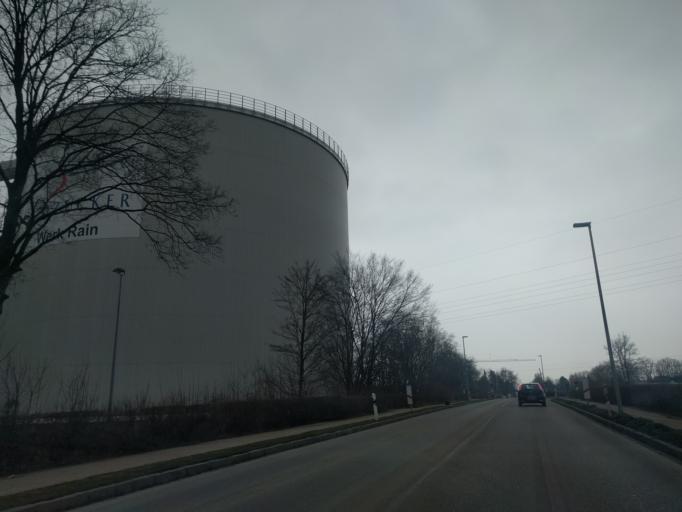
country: DE
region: Bavaria
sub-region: Swabia
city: Rain
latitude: 48.6972
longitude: 10.9072
